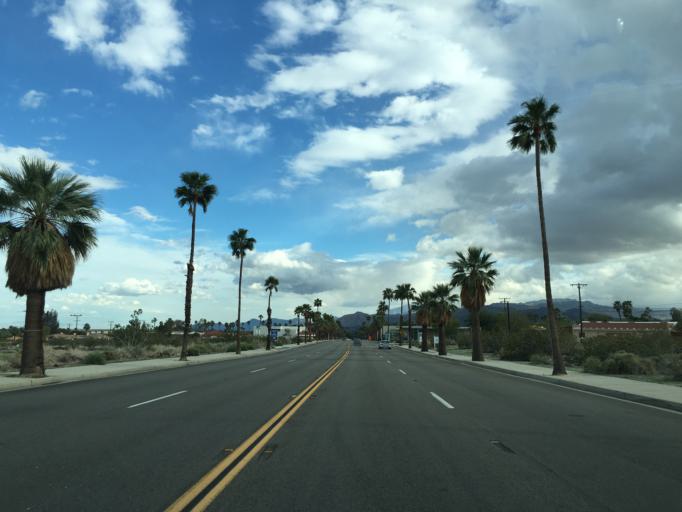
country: US
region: California
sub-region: Riverside County
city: Palm Springs
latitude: 33.8553
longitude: -116.5545
